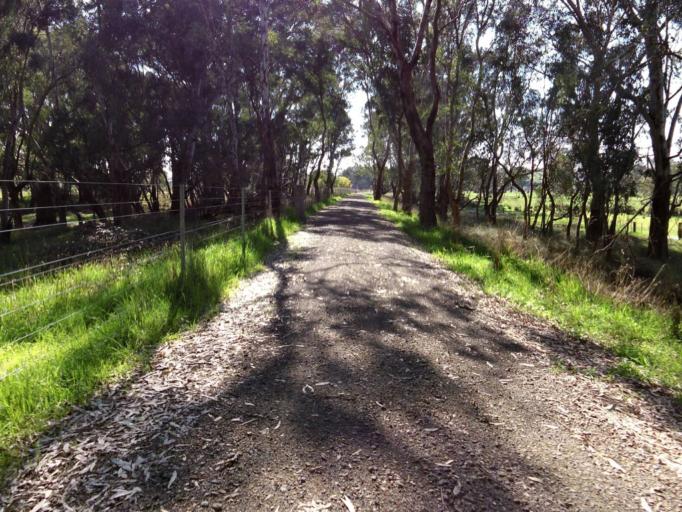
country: AU
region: Victoria
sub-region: Murrindindi
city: Alexandra
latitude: -37.1540
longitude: 145.5762
